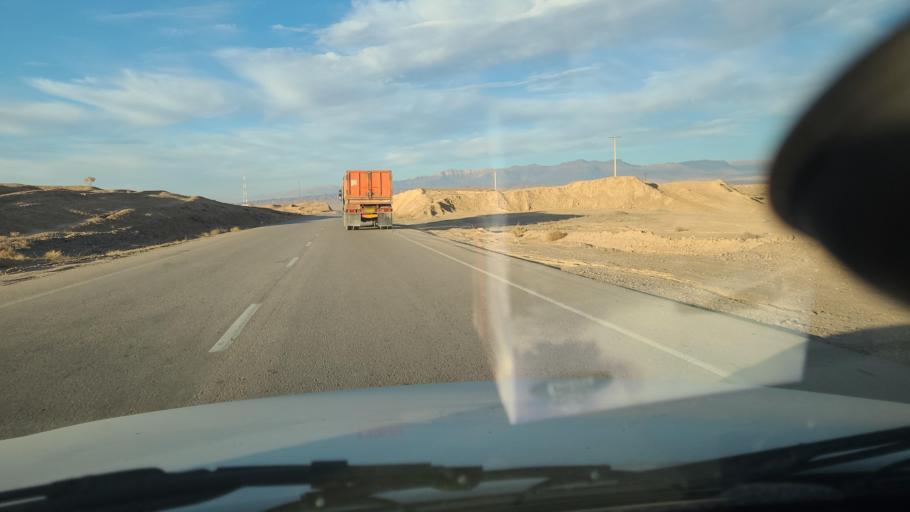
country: IR
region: Razavi Khorasan
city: Neqab
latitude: 36.7663
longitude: 57.5879
